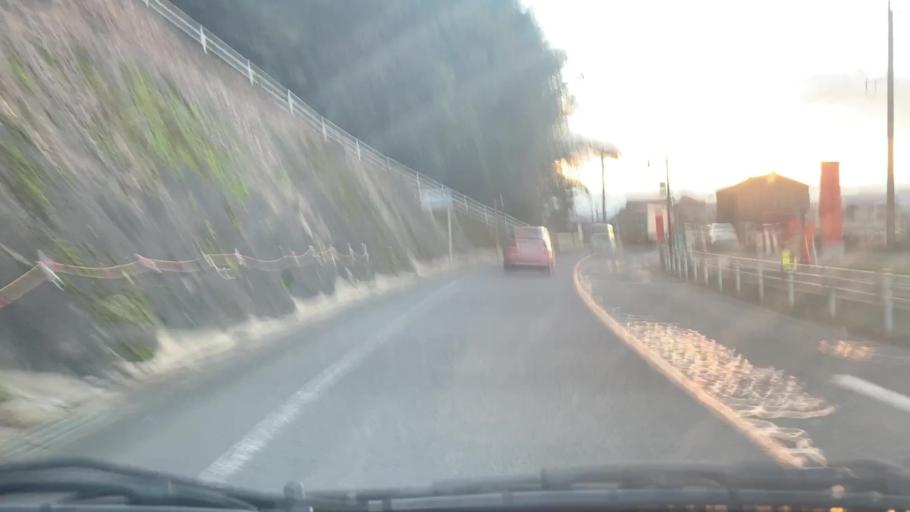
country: JP
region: Saga Prefecture
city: Takeocho-takeo
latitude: 33.2056
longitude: 130.0571
